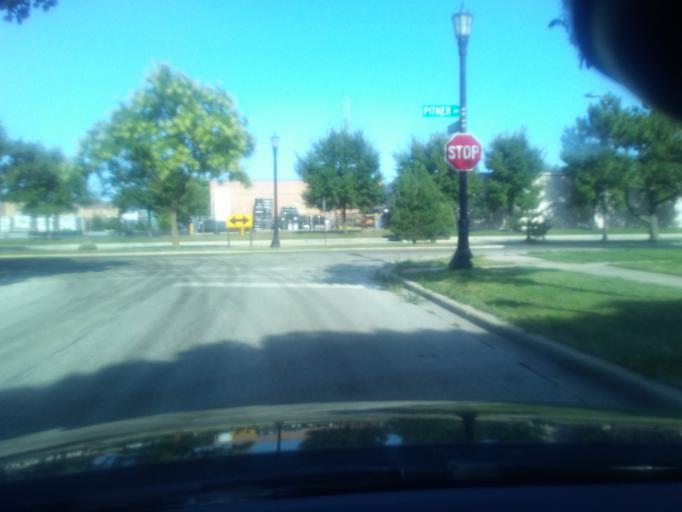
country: US
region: Illinois
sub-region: Cook County
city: Evanston
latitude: 42.0364
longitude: -87.7057
